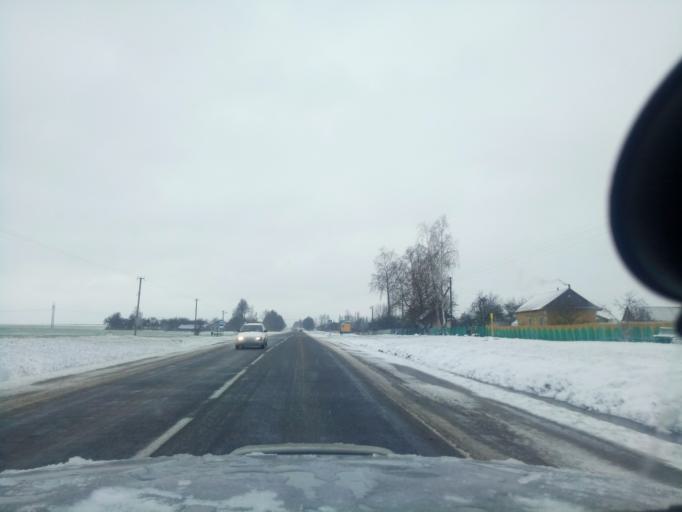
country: BY
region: Minsk
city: Klyetsk
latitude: 53.1156
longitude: 26.6623
